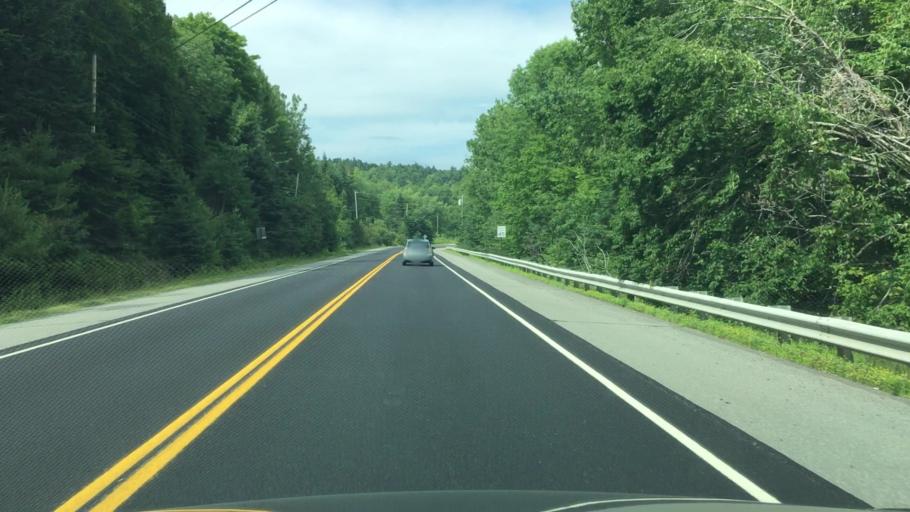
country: US
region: Maine
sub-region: Hancock County
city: Bucksport
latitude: 44.5518
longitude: -68.8099
